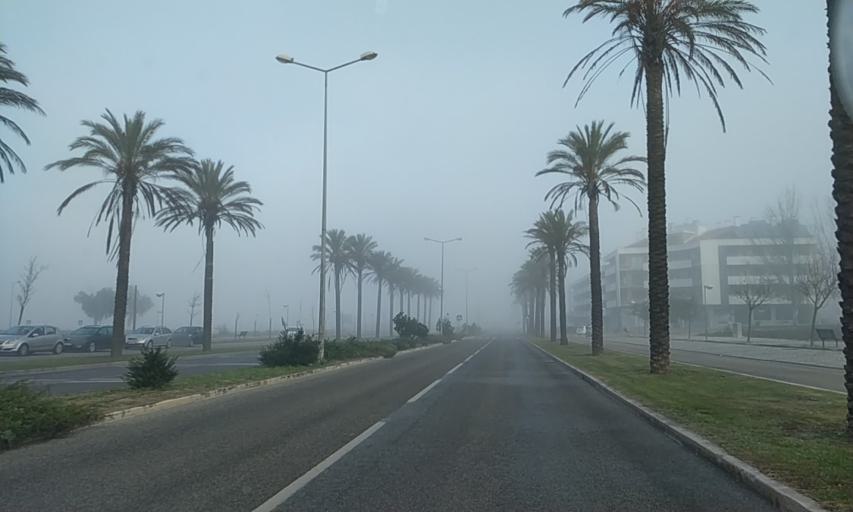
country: PT
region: Setubal
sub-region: Palmela
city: Pinhal Novo
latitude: 38.6216
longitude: -8.9186
